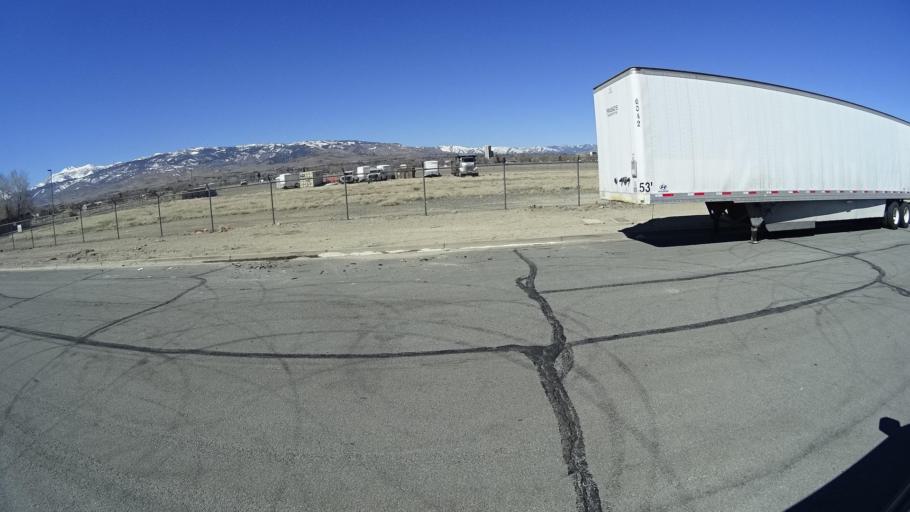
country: US
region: Nevada
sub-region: Washoe County
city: Sparks
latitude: 39.4867
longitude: -119.7642
